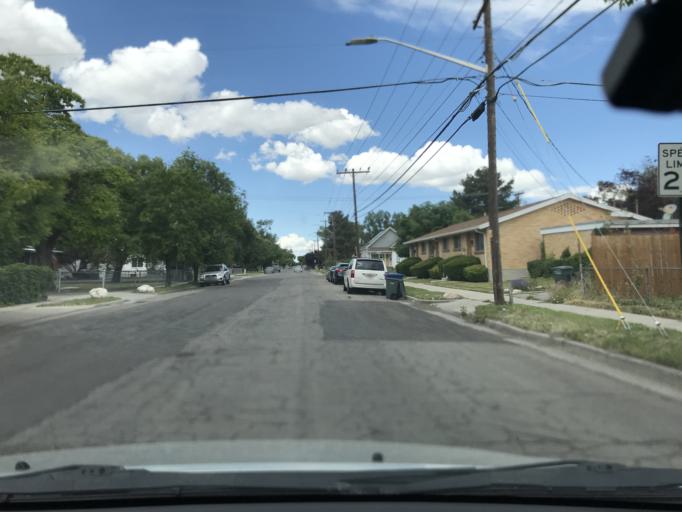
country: US
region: Utah
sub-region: Salt Lake County
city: Salt Lake City
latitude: 40.7802
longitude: -111.9302
